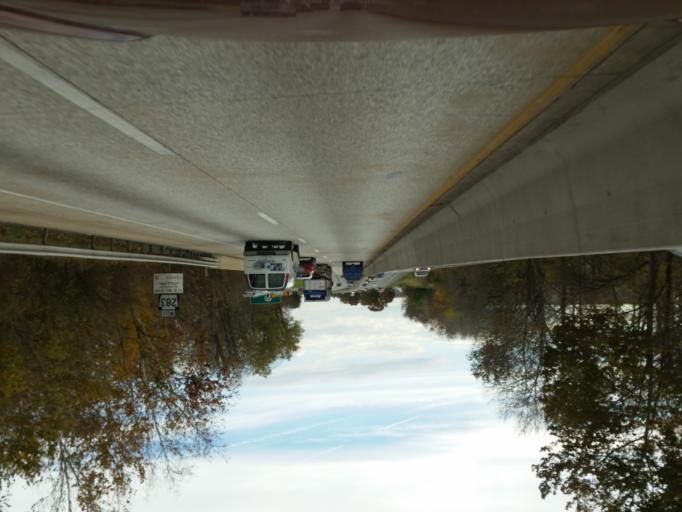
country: US
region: Pennsylvania
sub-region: Lancaster County
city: Salunga
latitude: 40.1092
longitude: -76.4375
